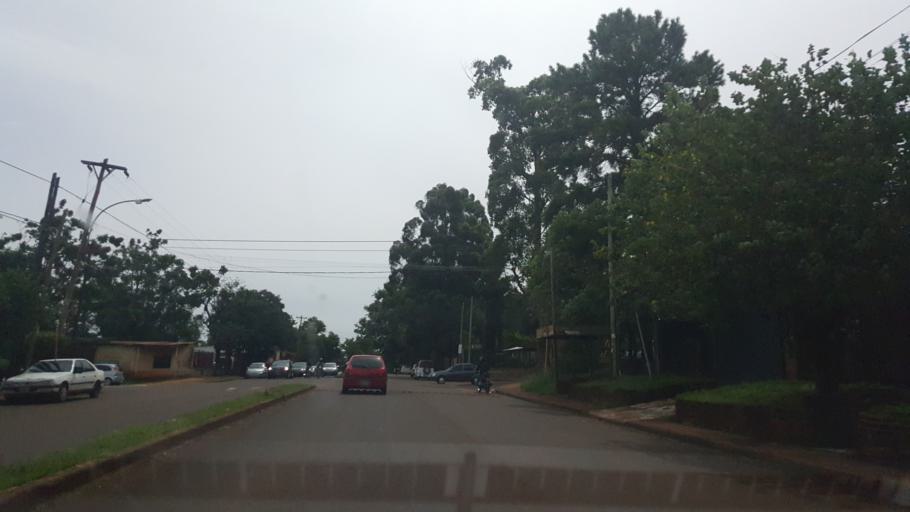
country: AR
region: Misiones
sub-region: Departamento de Capital
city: Posadas
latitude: -27.3970
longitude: -55.9435
